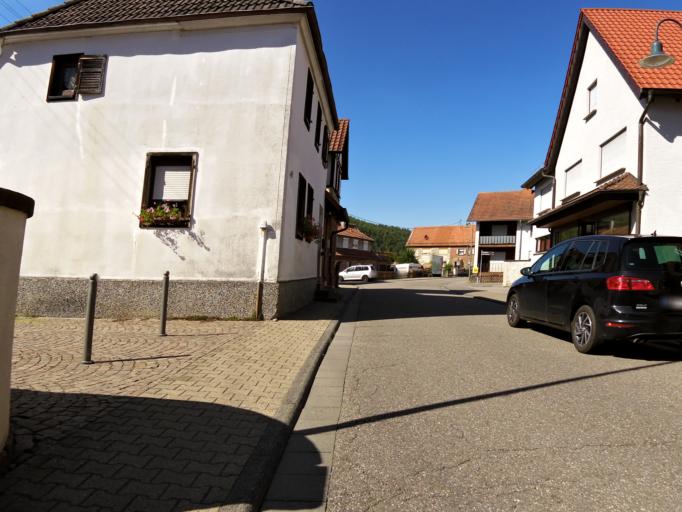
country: DE
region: Rheinland-Pfalz
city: Esthal
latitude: 49.3778
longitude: 7.9854
